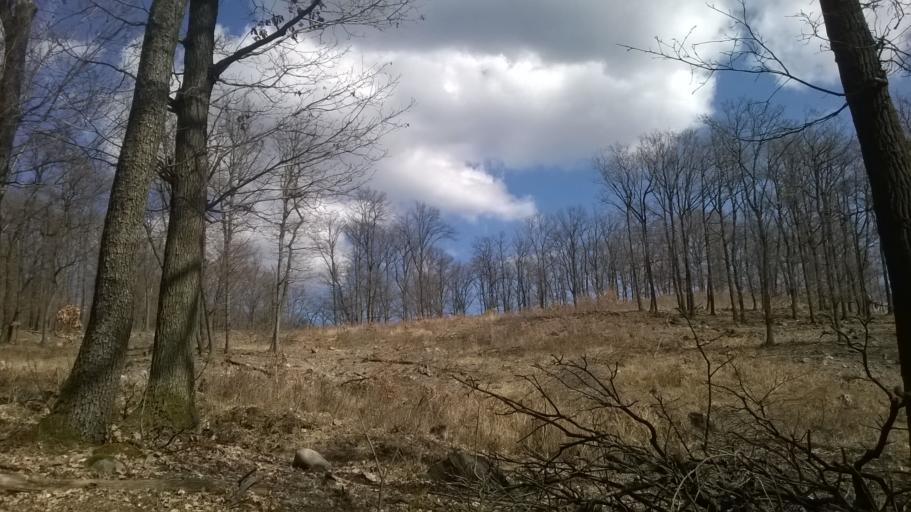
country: HU
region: Pest
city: Pilisszentkereszt
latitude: 47.6873
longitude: 18.9460
